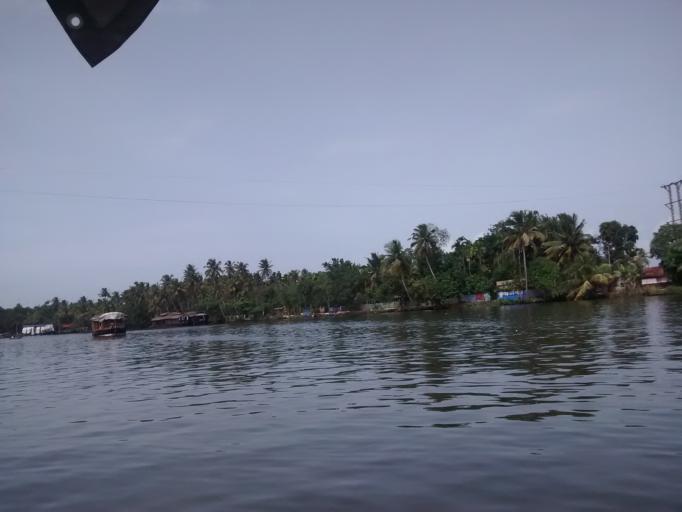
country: IN
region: Kerala
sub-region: Alappuzha
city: Alleppey
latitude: 9.4947
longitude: 76.3662
